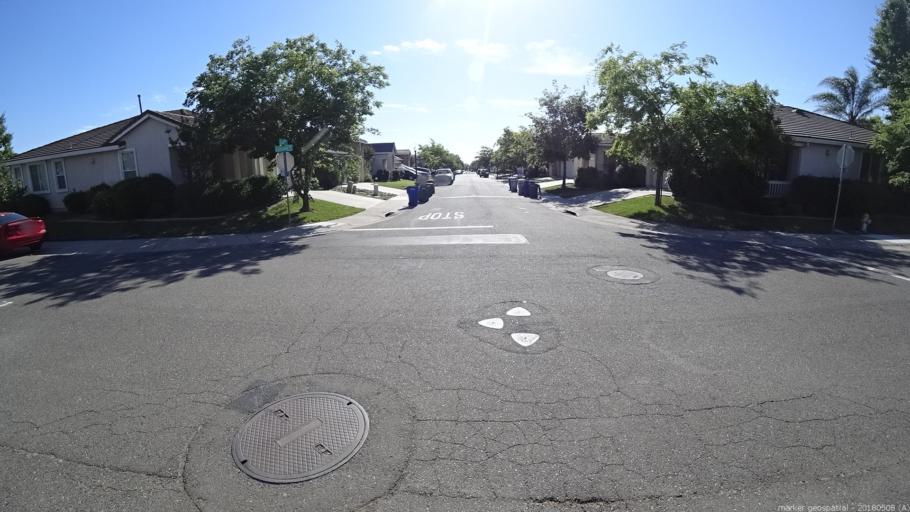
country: US
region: California
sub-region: Sacramento County
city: Elverta
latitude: 38.6834
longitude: -121.5031
